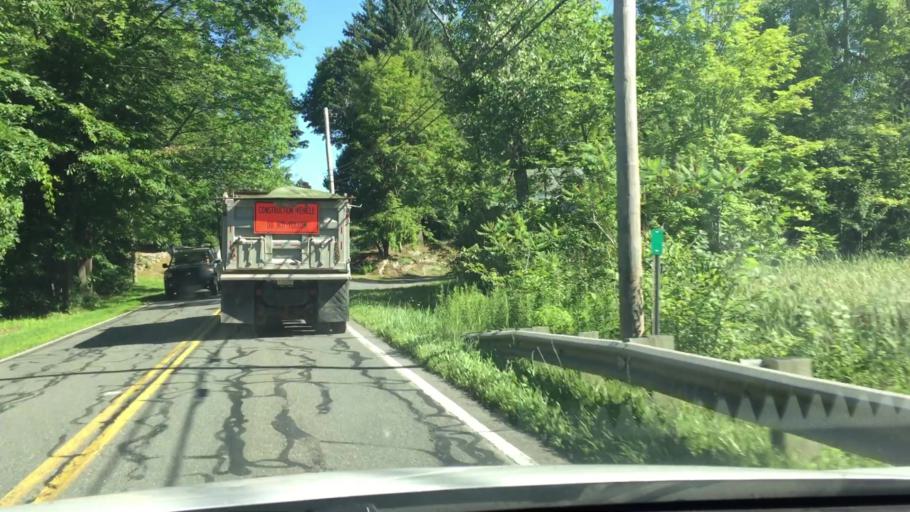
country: US
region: Massachusetts
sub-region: Berkshire County
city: West Stockbridge
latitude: 42.3230
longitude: -73.3678
